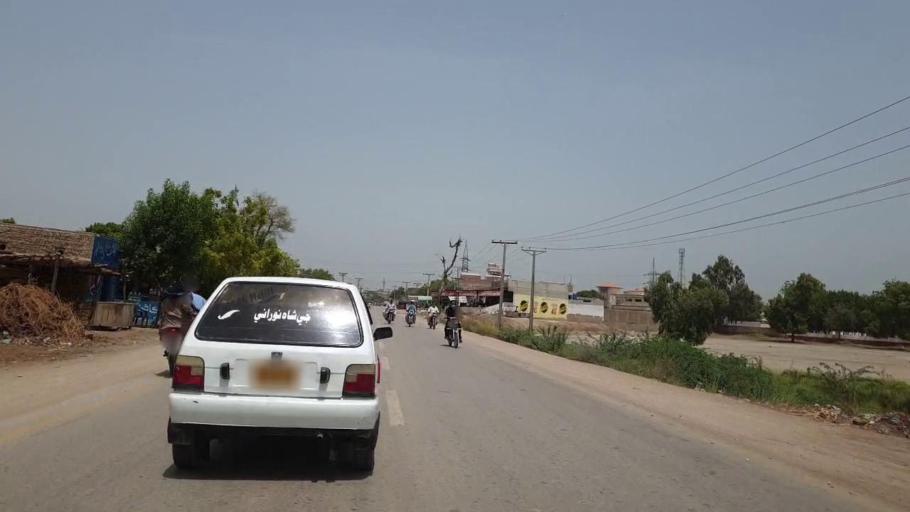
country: PK
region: Sindh
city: Nawabshah
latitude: 26.2486
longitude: 68.4297
